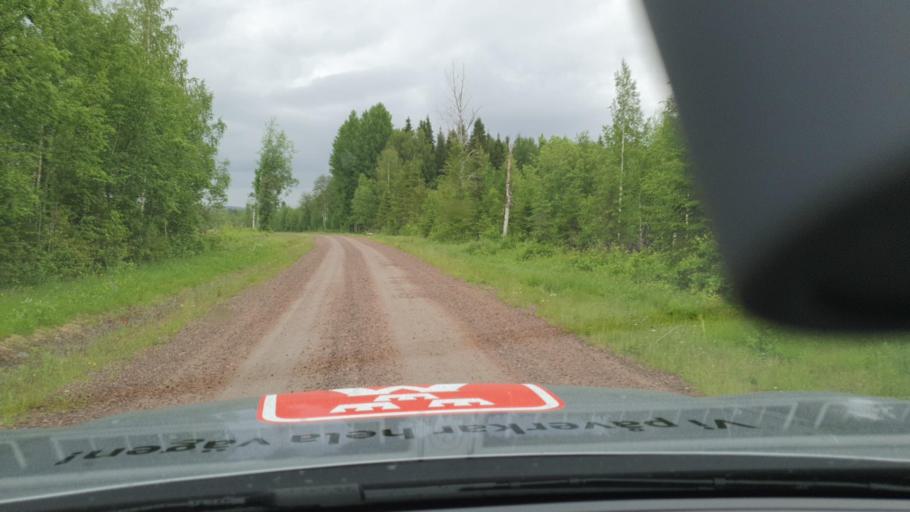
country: SE
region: Norrbotten
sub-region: Overkalix Kommun
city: OEverkalix
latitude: 66.6073
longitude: 22.7457
